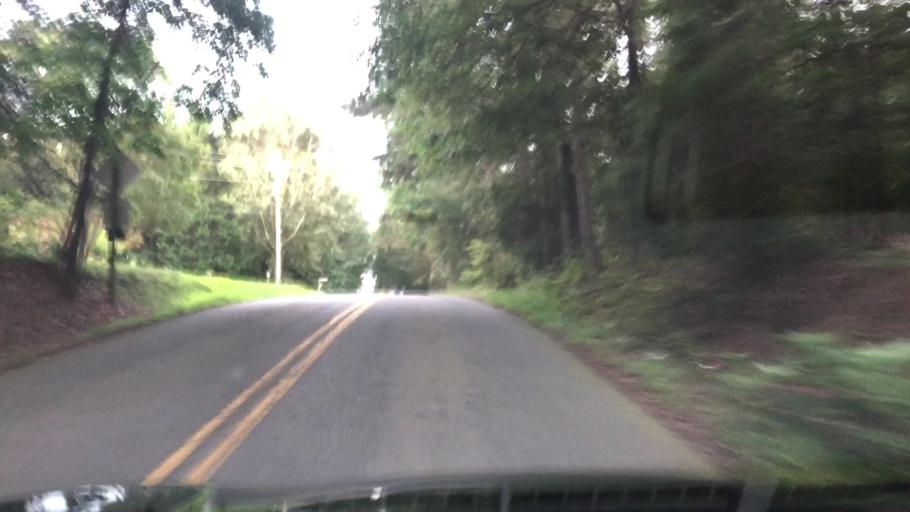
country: US
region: Virginia
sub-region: Fauquier County
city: Bealeton
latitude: 38.5128
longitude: -77.6845
